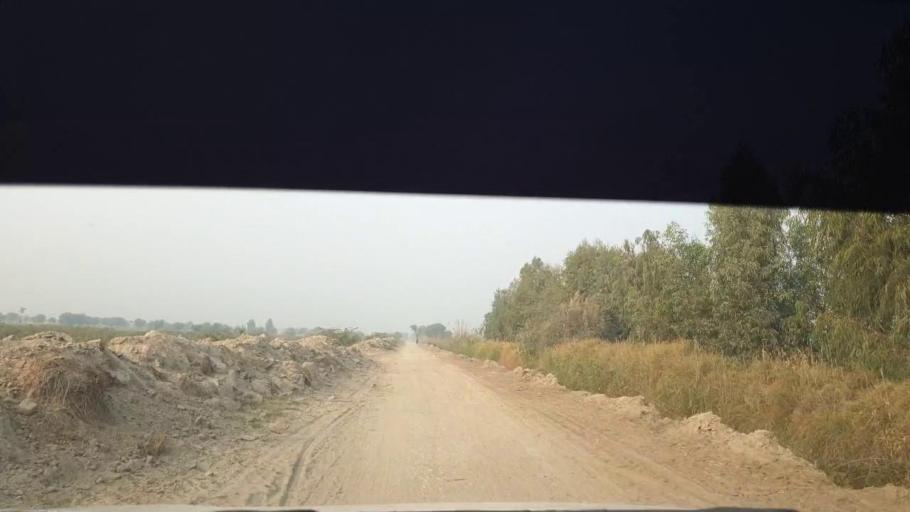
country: PK
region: Sindh
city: Berani
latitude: 25.8332
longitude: 68.8912
